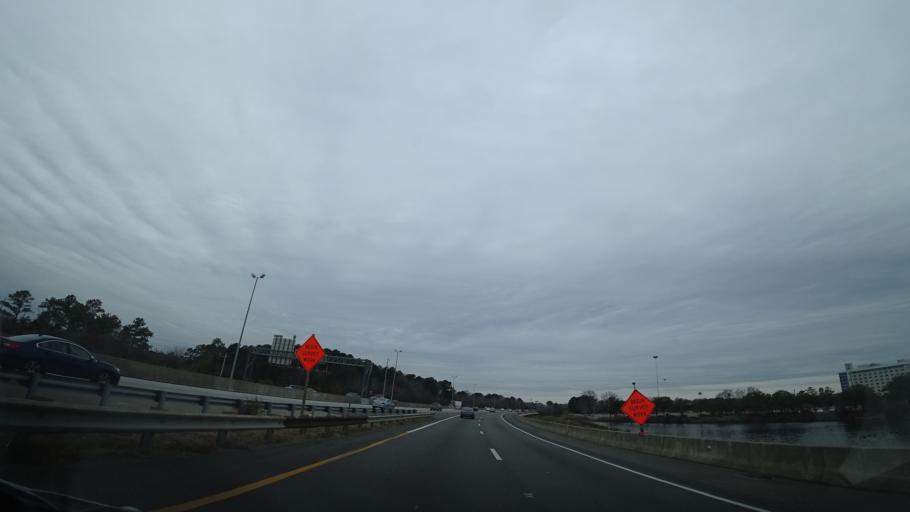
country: US
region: Virginia
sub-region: City of Hampton
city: Hampton
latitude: 37.0332
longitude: -76.3820
